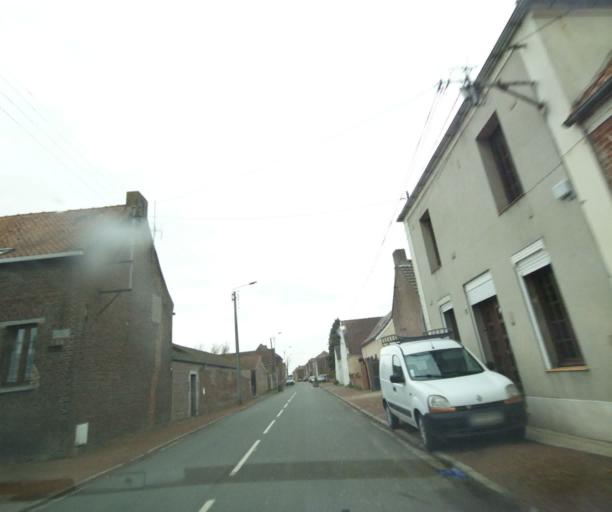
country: FR
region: Nord-Pas-de-Calais
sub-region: Departement du Nord
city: Vicq
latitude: 50.4099
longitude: 3.6079
